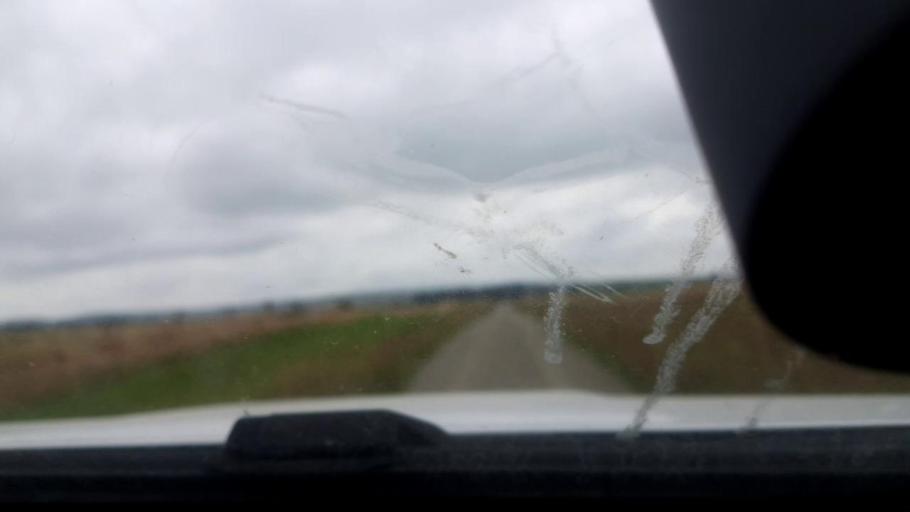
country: NZ
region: Canterbury
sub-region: Timaru District
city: Pleasant Point
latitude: -44.2320
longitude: 171.1669
